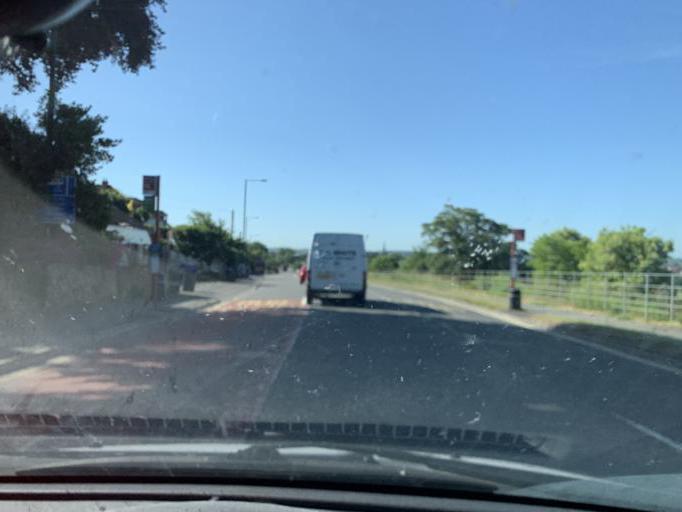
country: GB
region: England
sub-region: Wiltshire
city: Salisbury
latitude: 51.0905
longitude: -1.7998
